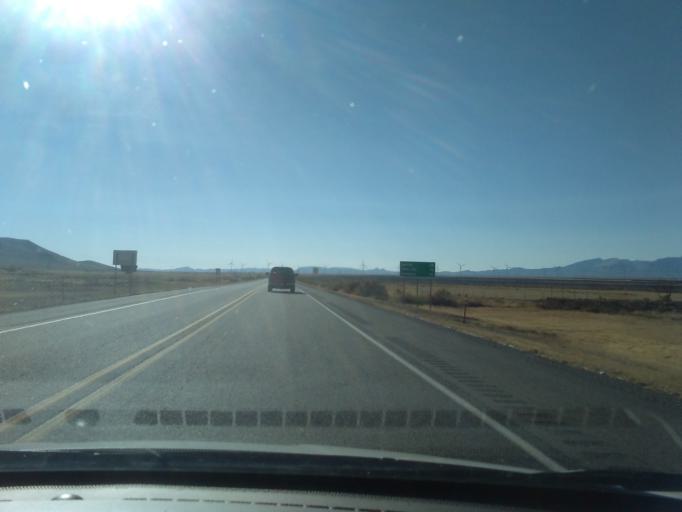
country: US
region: New Mexico
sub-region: Dona Ana County
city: Hatch
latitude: 32.5752
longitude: -107.4517
